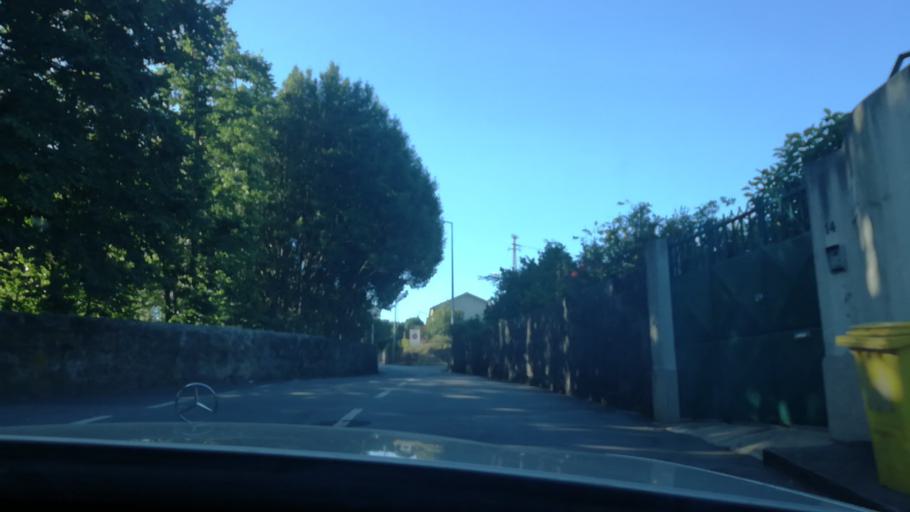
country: PT
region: Porto
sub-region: Maia
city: Leca do Bailio
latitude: 41.2210
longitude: -8.6237
